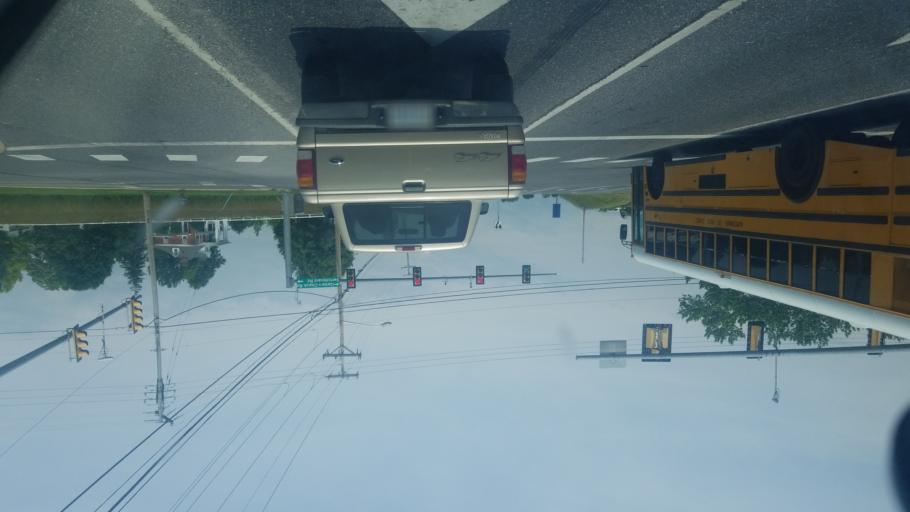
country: US
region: Virginia
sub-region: City of Harrisonburg
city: Harrisonburg
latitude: 38.4554
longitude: -78.8989
